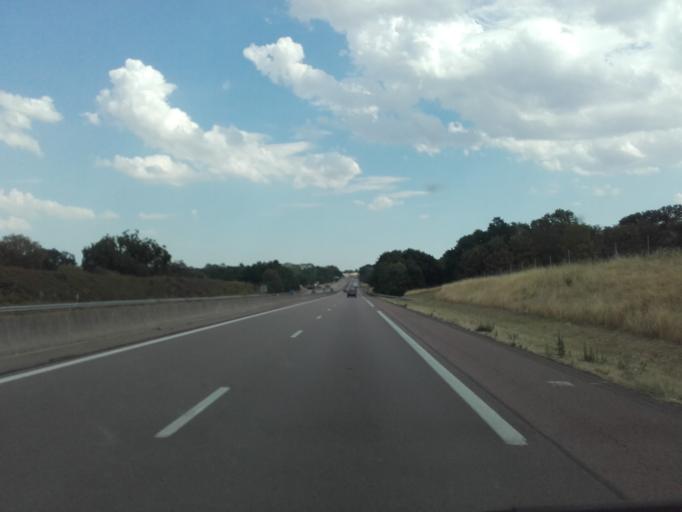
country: FR
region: Bourgogne
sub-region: Departement de l'Yonne
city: Avallon
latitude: 47.4972
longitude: 4.1164
